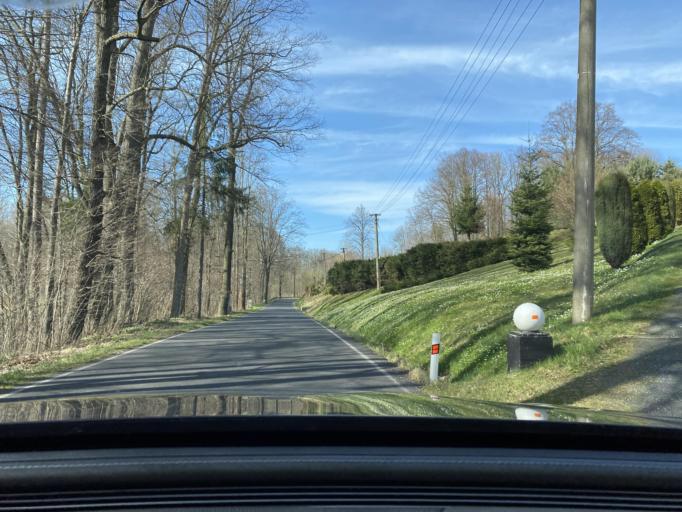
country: CZ
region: Ustecky
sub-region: Okres Decin
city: Sluknov
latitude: 51.0194
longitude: 14.4559
